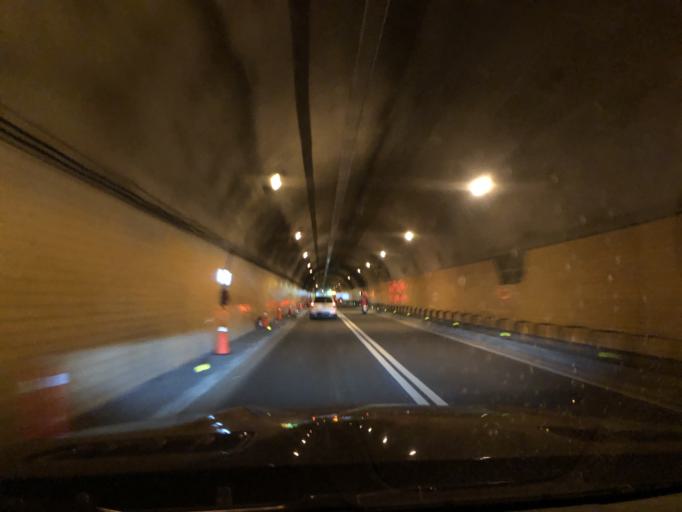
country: TW
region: Taipei
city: Taipei
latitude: 24.9942
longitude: 121.5516
